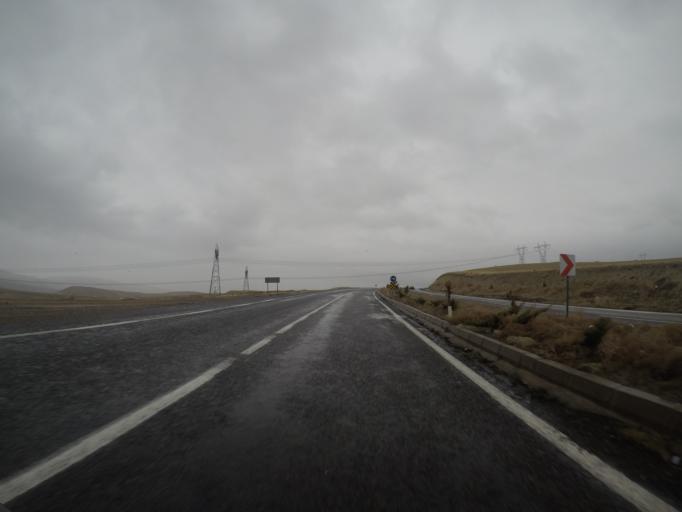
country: TR
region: Nevsehir
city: Avanos
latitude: 38.7078
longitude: 34.8765
